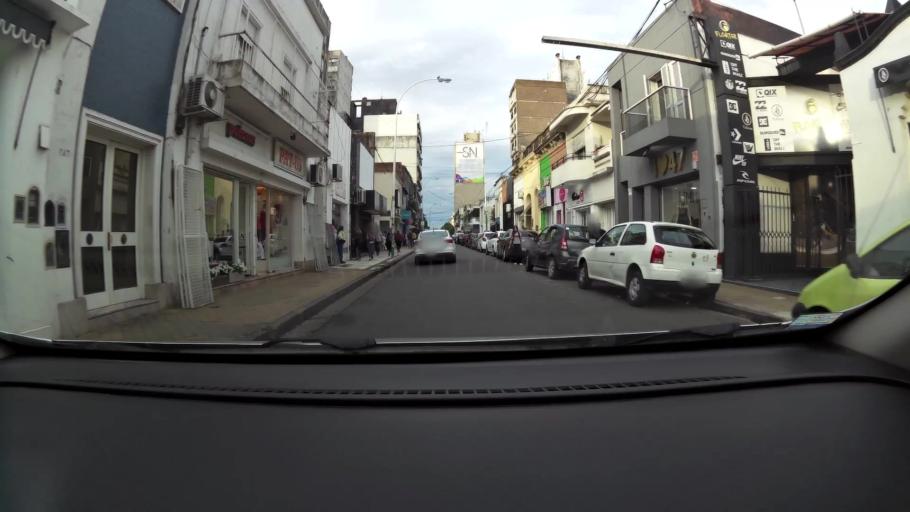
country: AR
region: Buenos Aires
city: San Nicolas de los Arroyos
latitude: -33.3293
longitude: -60.2177
